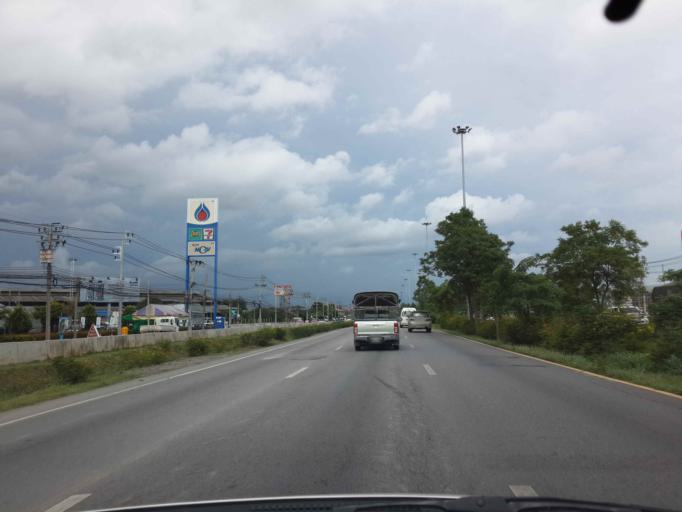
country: TH
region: Bangkok
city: Bang Bon
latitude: 13.6228
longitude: 100.3900
